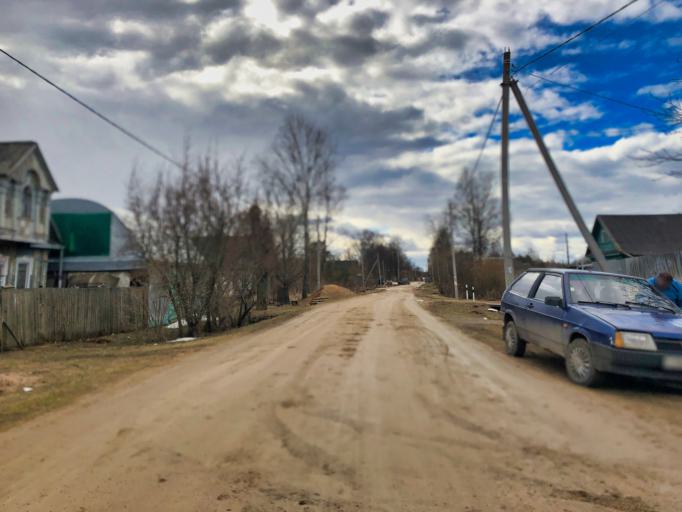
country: RU
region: Tverskaya
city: Rzhev
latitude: 56.2262
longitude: 34.3074
